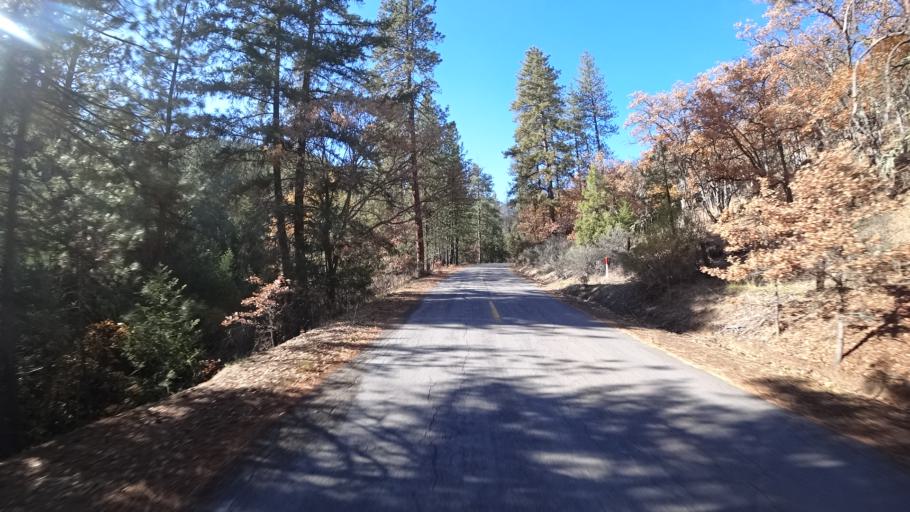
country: US
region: California
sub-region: Siskiyou County
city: Yreka
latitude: 41.7231
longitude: -122.6990
